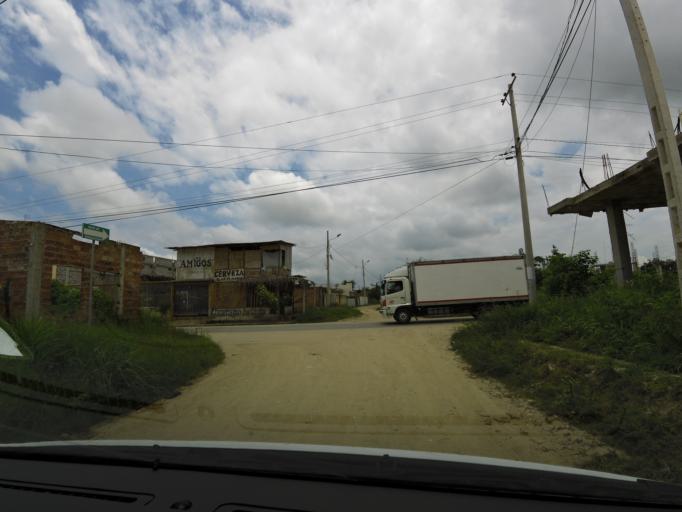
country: EC
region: El Oro
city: Huaquillas
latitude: -3.4867
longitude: -80.2167
